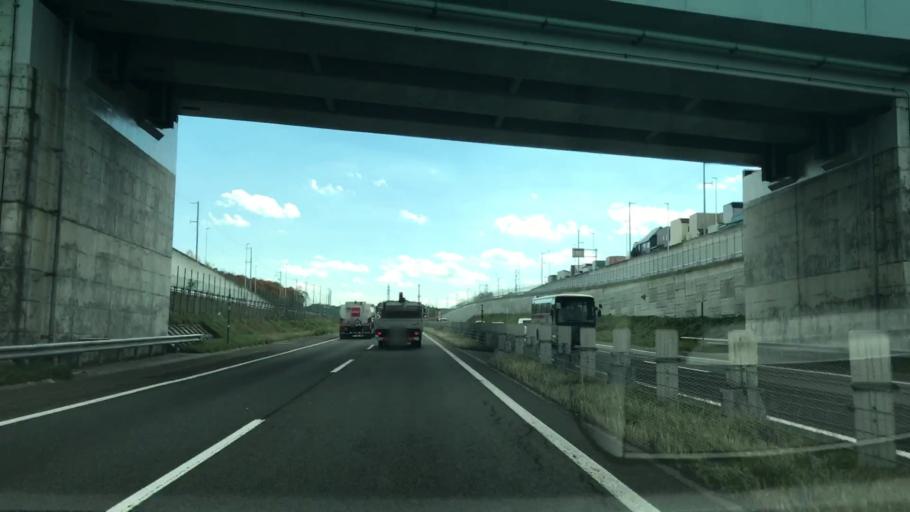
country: JP
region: Hokkaido
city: Kitahiroshima
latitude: 42.9929
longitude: 141.4693
